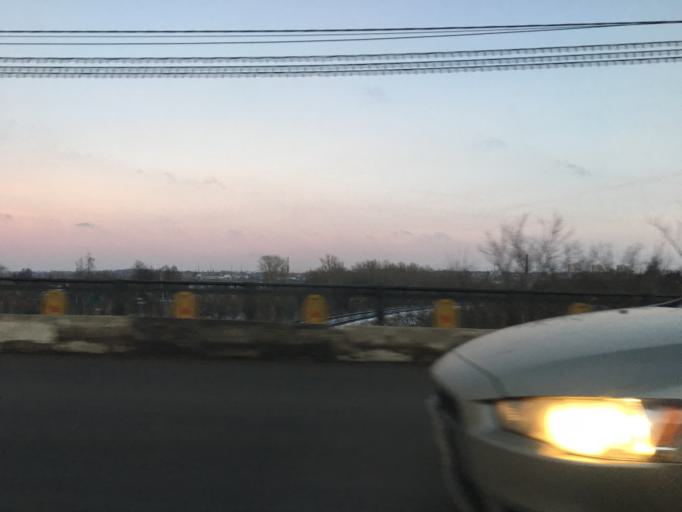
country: RU
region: Tula
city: Tula
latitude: 54.2215
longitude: 37.6265
